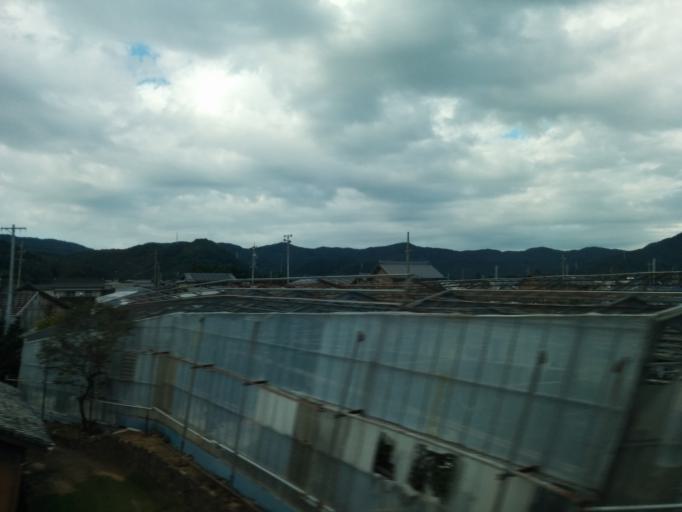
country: JP
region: Aichi
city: Gamagori
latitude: 34.8372
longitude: 137.2198
